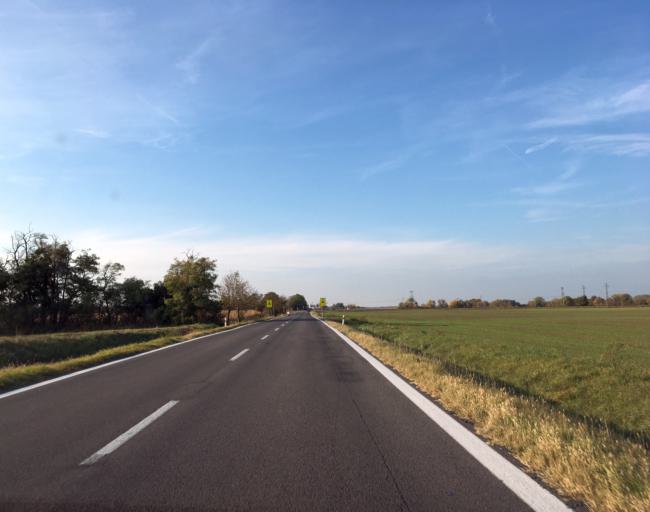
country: SK
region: Nitriansky
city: Surany
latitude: 48.0565
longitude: 18.1050
